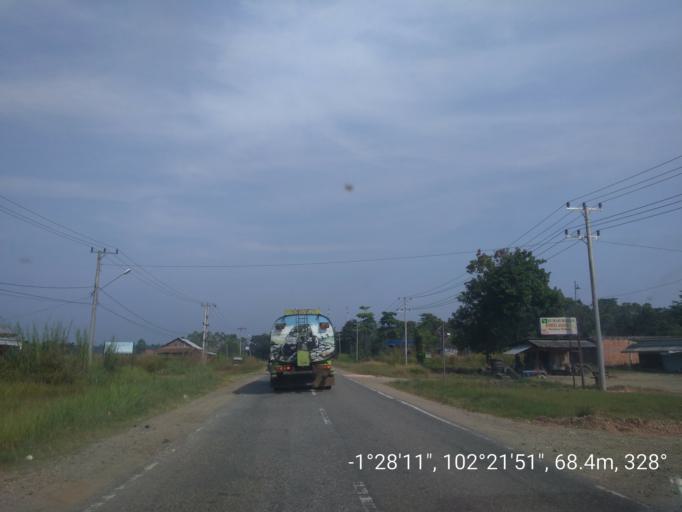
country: ID
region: Jambi
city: Muara Tebo
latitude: -1.4699
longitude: 102.3647
